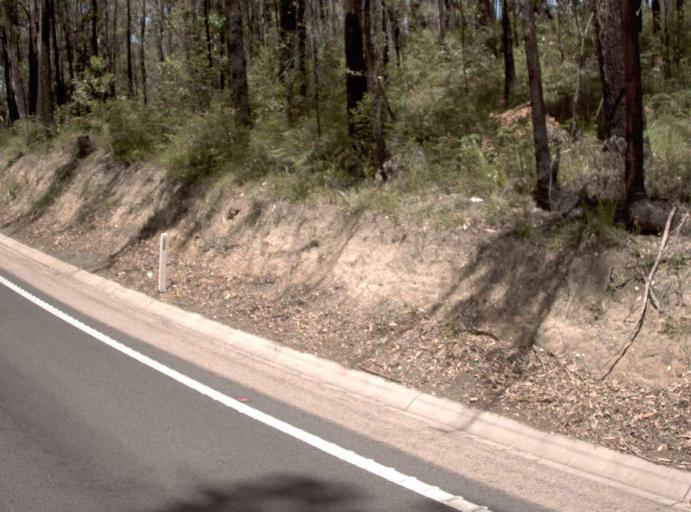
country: AU
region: Victoria
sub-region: East Gippsland
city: Lakes Entrance
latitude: -37.6945
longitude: 148.7262
